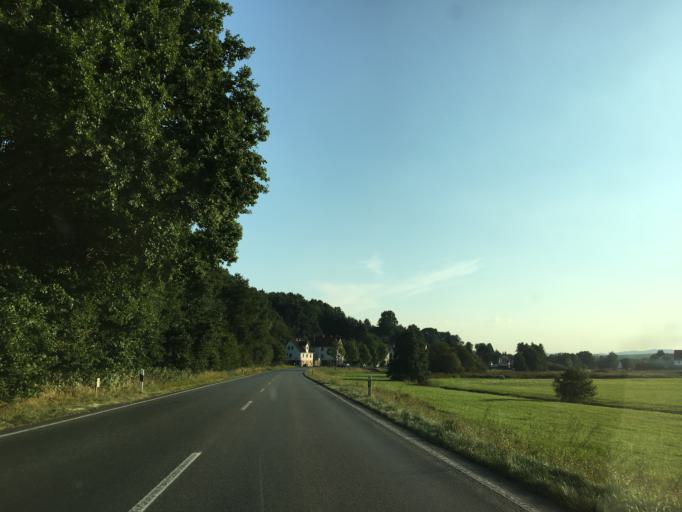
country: DE
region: Hesse
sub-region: Regierungsbezirk Giessen
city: Munchhausen
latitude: 50.9675
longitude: 8.7235
